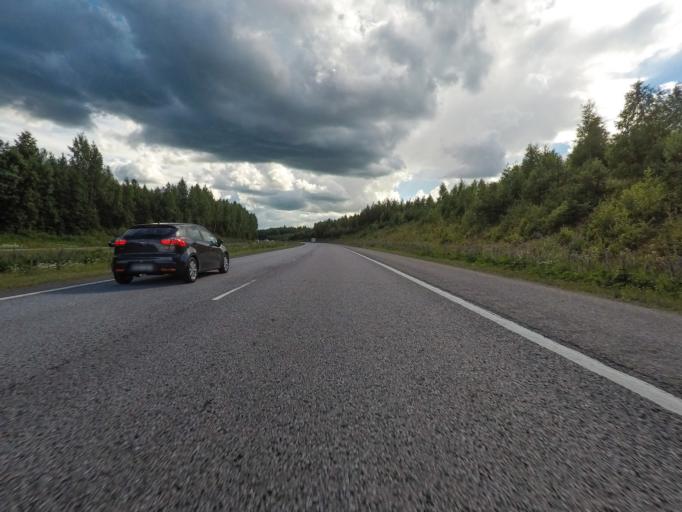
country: FI
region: Paijanne Tavastia
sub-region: Lahti
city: Nastola
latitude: 61.0281
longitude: 25.8337
